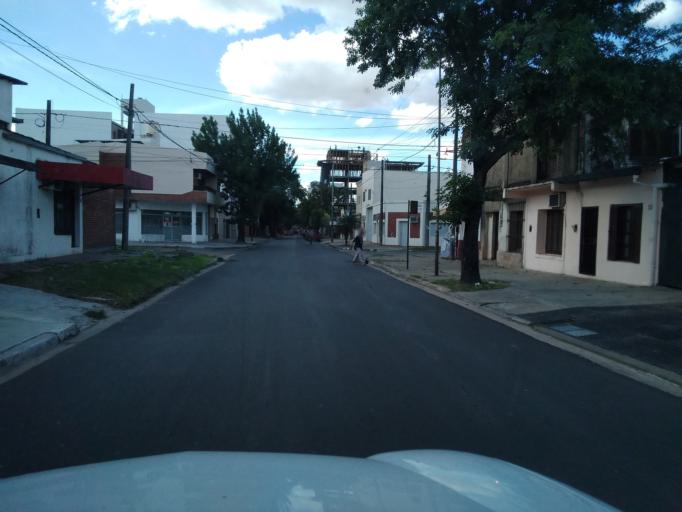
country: AR
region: Corrientes
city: Corrientes
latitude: -27.4798
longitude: -58.8370
